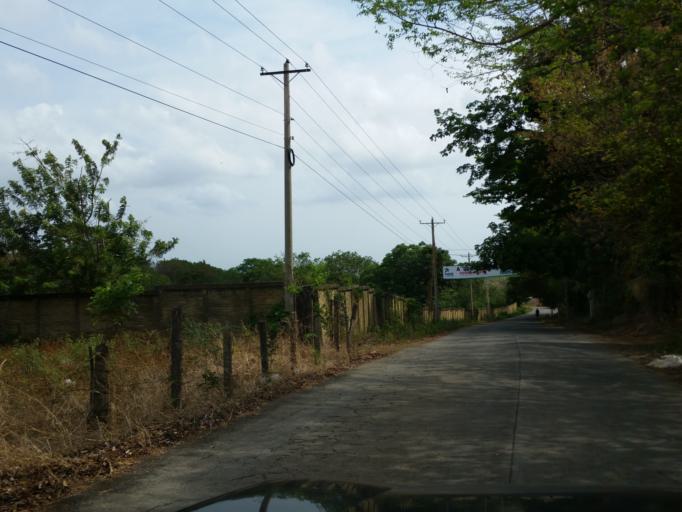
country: NI
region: Masaya
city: Ticuantepe
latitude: 12.0656
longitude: -86.2492
